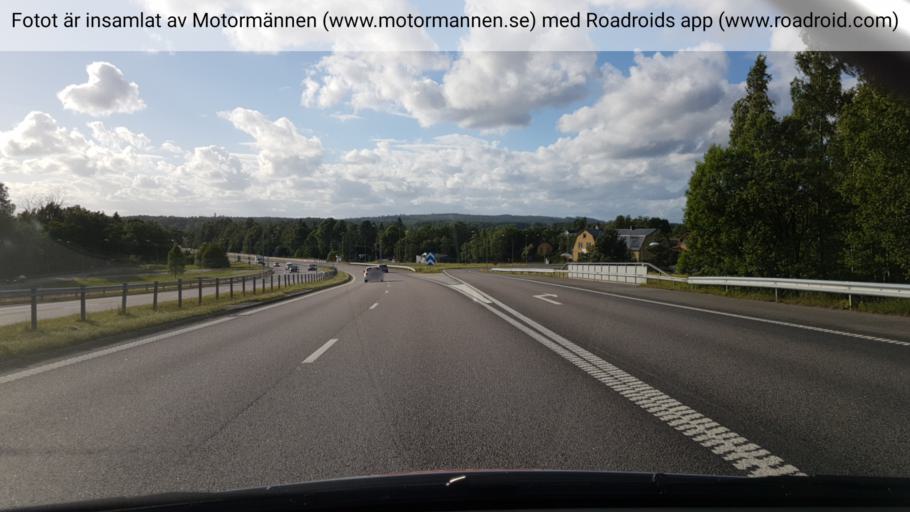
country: SE
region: OErebro
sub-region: Karlskoga Kommun
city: Karlskoga
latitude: 59.3203
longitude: 14.5938
